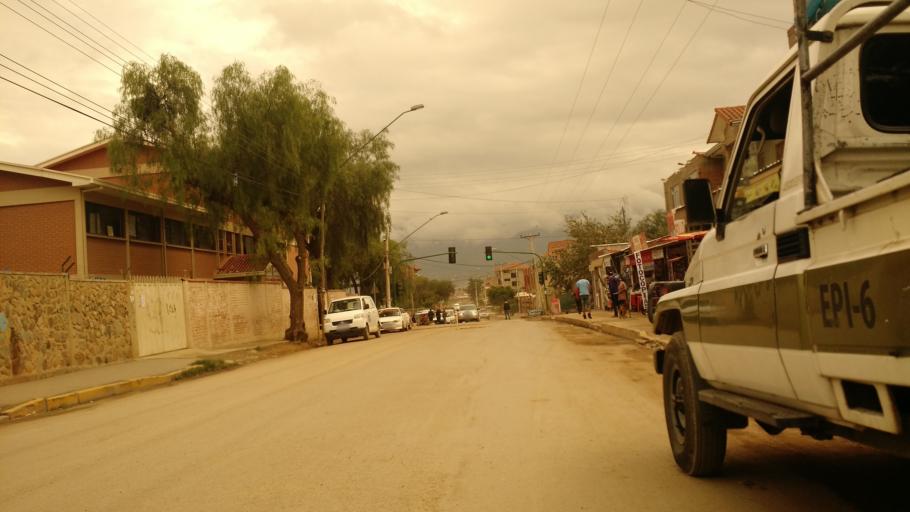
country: BO
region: Cochabamba
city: Cochabamba
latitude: -17.4478
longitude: -66.1555
